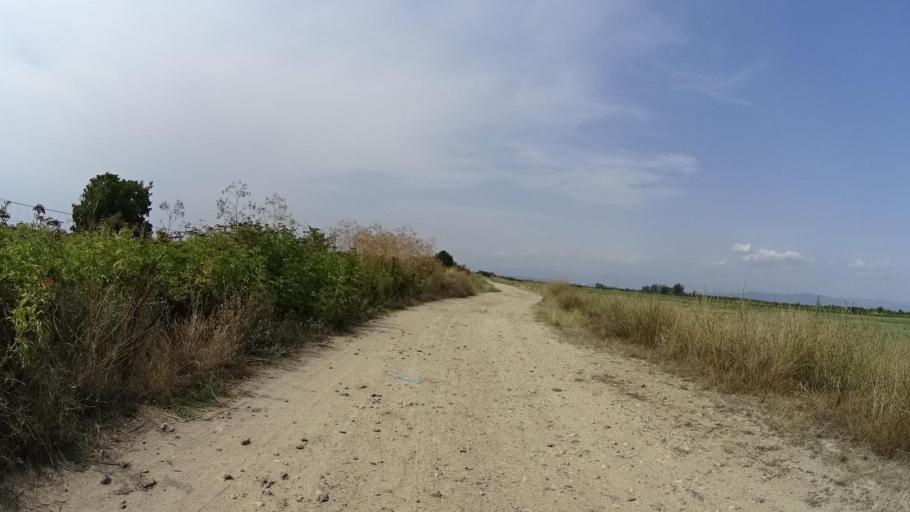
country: BG
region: Plovdiv
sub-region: Obshtina Kaloyanovo
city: Kaloyanovo
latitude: 42.2886
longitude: 24.7972
